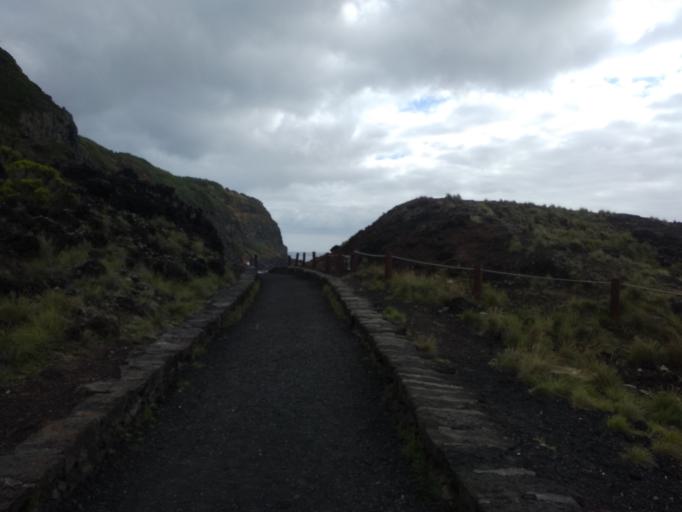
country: PT
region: Azores
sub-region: Ponta Delgada
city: Arrifes
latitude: 37.8599
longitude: -25.8525
